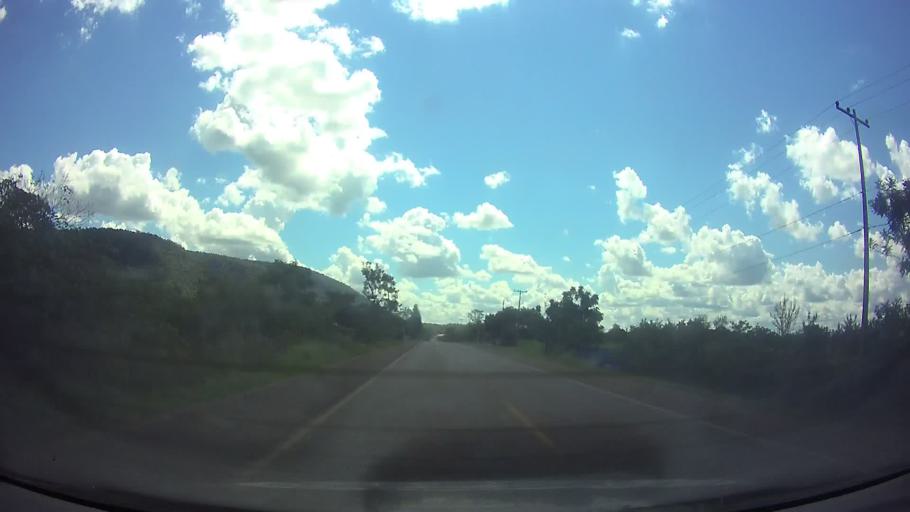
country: PY
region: Paraguari
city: La Colmena
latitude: -25.9186
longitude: -56.7259
